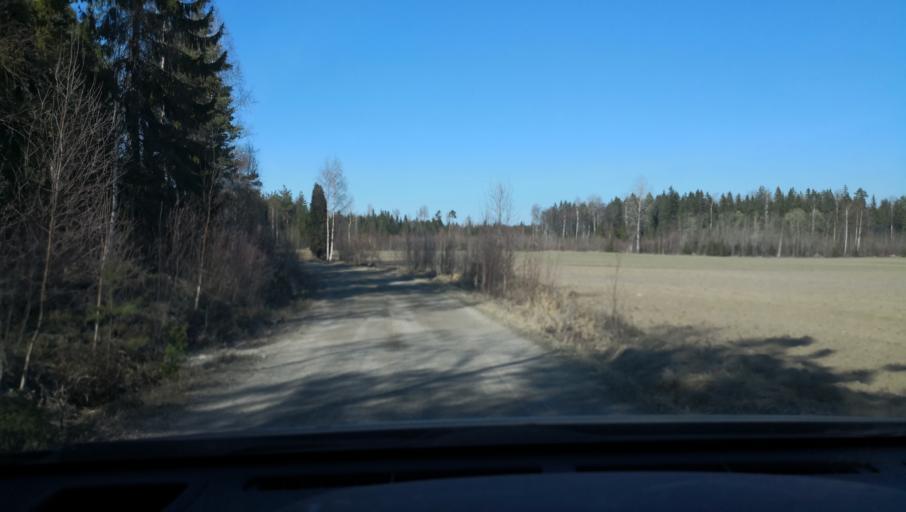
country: SE
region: Vaestmanland
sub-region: Sala Kommun
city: Sala
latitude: 59.9311
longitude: 16.4510
